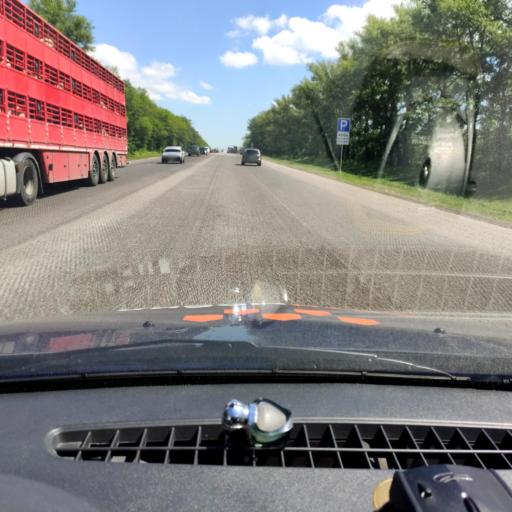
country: RU
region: Orjol
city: Zmiyevka
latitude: 52.7092
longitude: 36.3565
